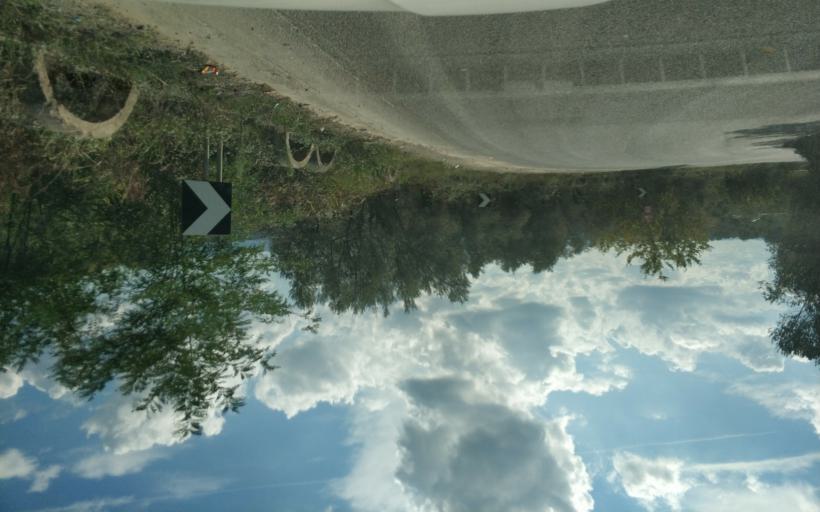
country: AL
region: Durres
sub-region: Rrethi i Krujes
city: Kruje
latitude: 41.4836
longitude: 19.7657
